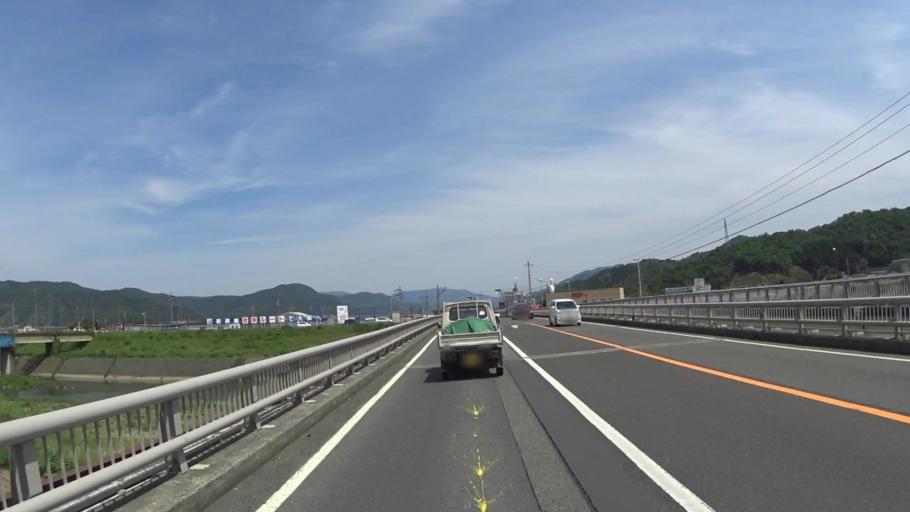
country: JP
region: Fukui
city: Obama
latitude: 35.4888
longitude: 135.7562
